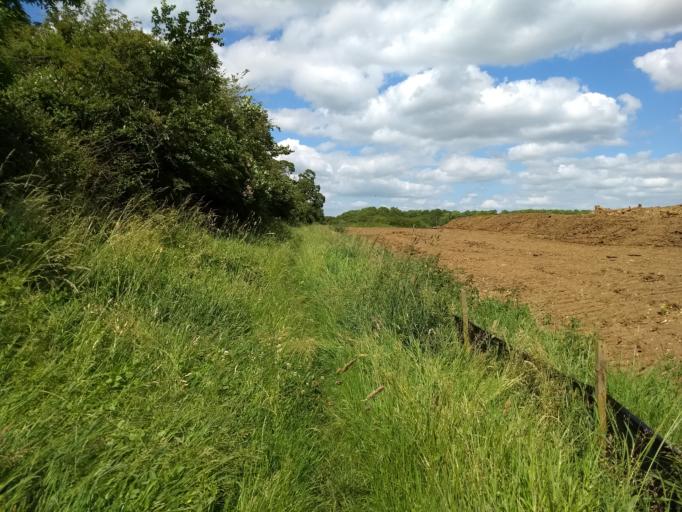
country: GB
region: England
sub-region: Milton Keynes
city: Calverton
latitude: 52.0471
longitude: -0.8435
